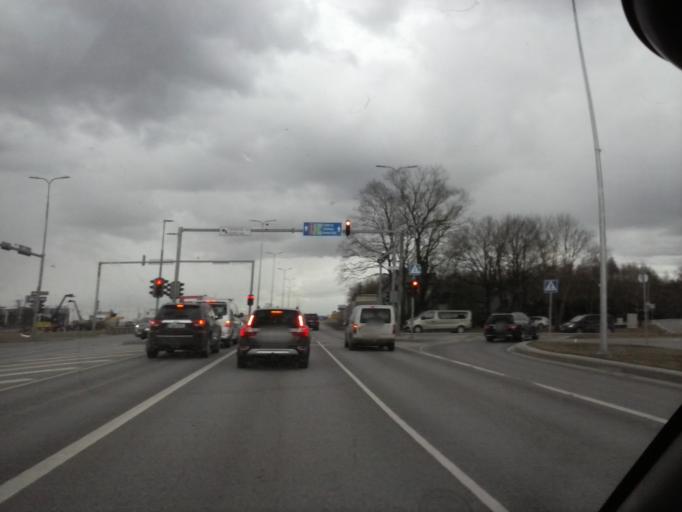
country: EE
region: Harju
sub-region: Tallinna linn
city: Tallinn
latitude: 59.4027
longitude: 24.8132
